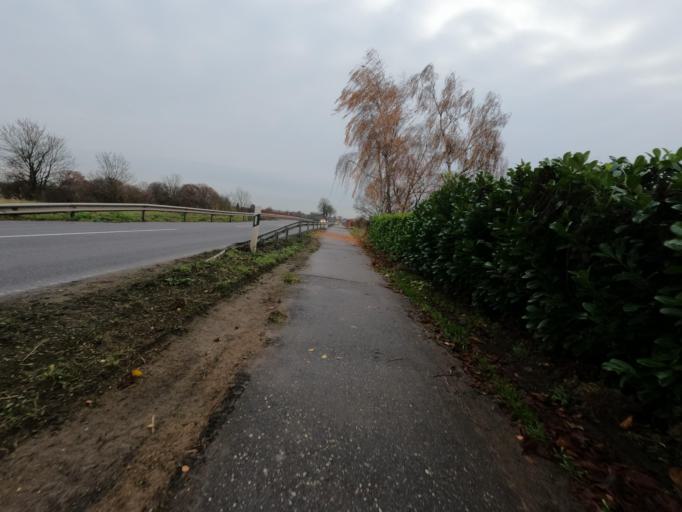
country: DE
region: North Rhine-Westphalia
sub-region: Regierungsbezirk Koln
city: Heinsberg
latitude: 51.0534
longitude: 6.1047
